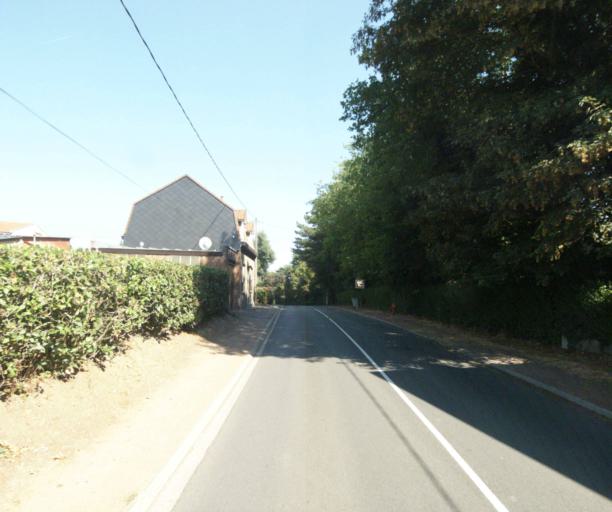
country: FR
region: Nord-Pas-de-Calais
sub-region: Departement du Nord
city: Wervicq-Sud
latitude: 50.7620
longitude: 3.0480
